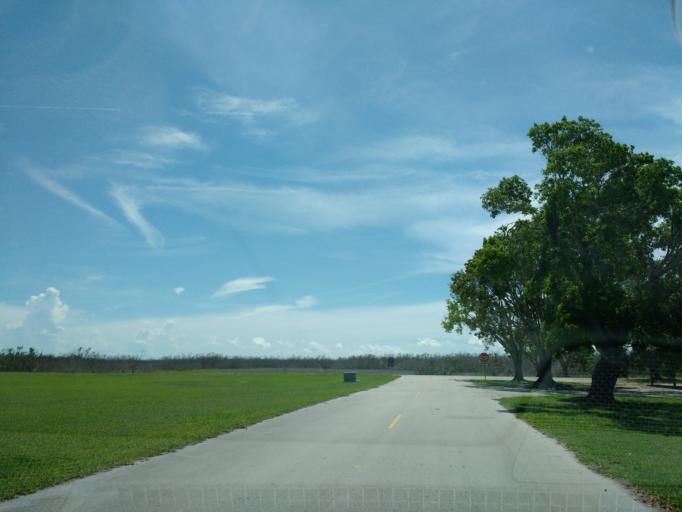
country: US
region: Florida
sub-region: Monroe County
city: Islamorada
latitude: 25.1446
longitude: -80.9242
